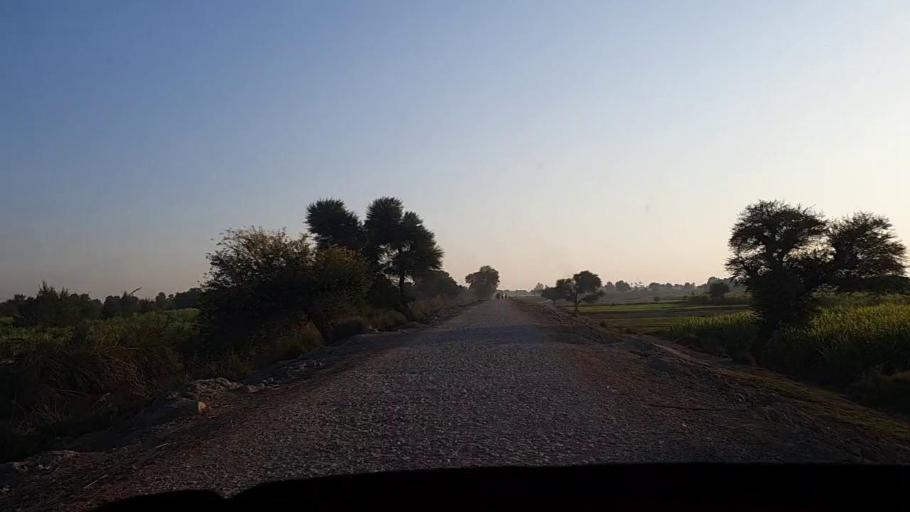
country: PK
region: Sindh
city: Sobhadero
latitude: 27.3713
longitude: 68.3781
